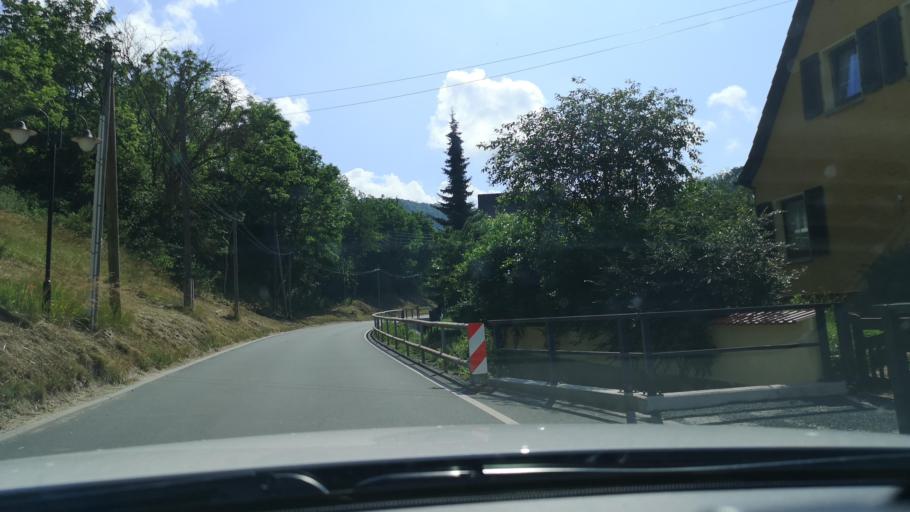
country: DE
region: Thuringia
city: Tautenburg
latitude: 51.0111
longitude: 11.6990
